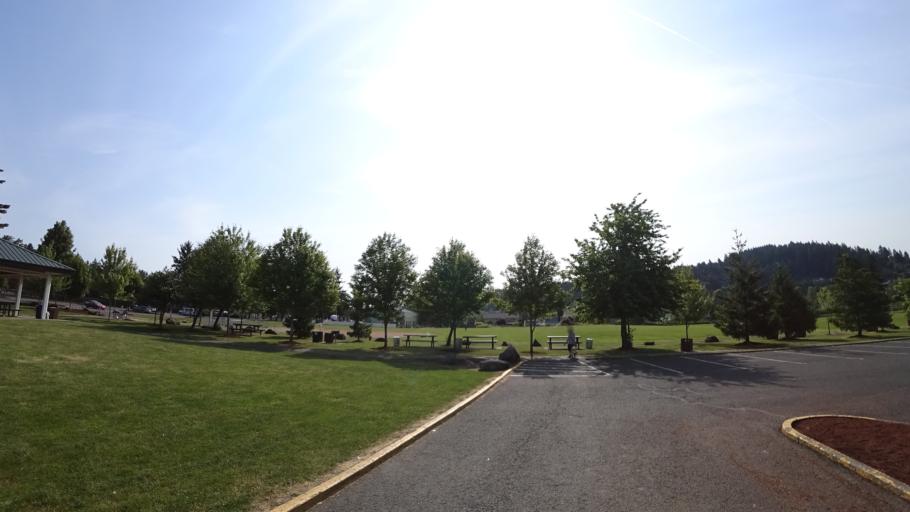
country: US
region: Oregon
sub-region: Clackamas County
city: Happy Valley
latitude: 45.4529
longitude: -122.5215
